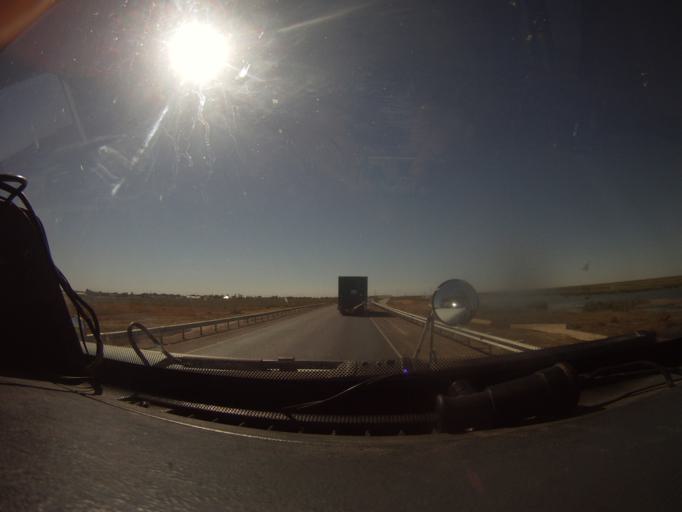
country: KZ
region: Qyzylorda
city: Zhosaly
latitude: 45.4802
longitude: 64.0611
